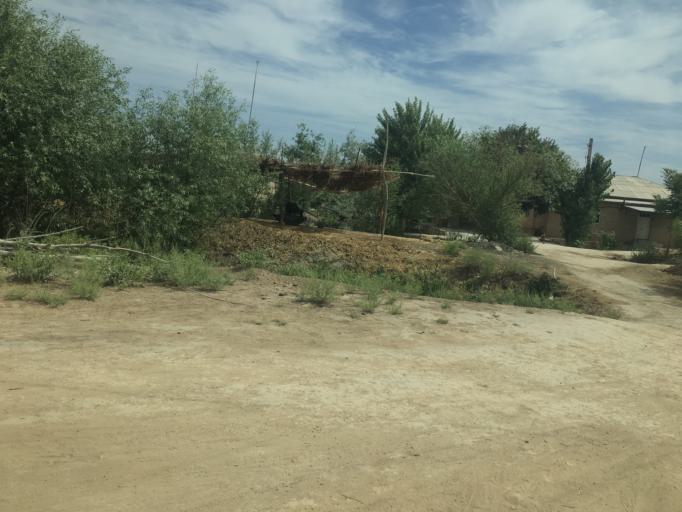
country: TM
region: Dasoguz
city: Tagta
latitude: 41.6003
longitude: 59.8537
